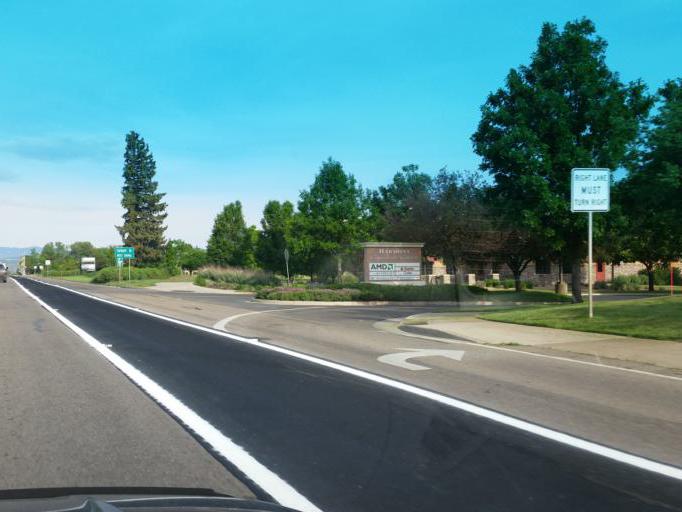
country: US
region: Colorado
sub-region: Larimer County
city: Fort Collins
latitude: 40.5234
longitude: -105.0231
